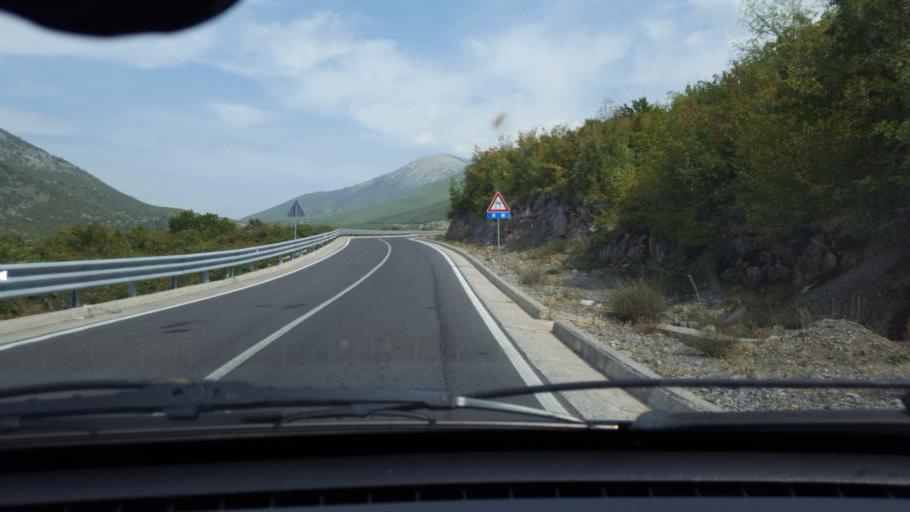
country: AL
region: Shkoder
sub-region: Rrethi i Malesia e Madhe
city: Kastrat
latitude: 42.3703
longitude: 19.4716
